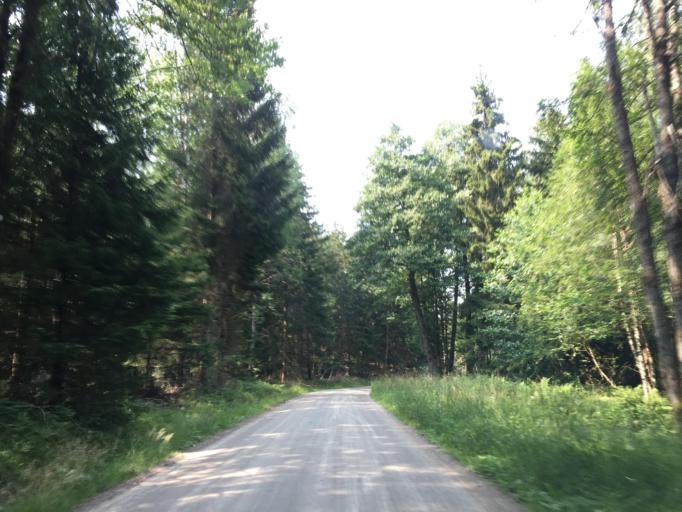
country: SE
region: Vaestra Goetaland
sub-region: Lilla Edets Kommun
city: Lilla Edet
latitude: 58.2274
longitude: 12.1215
